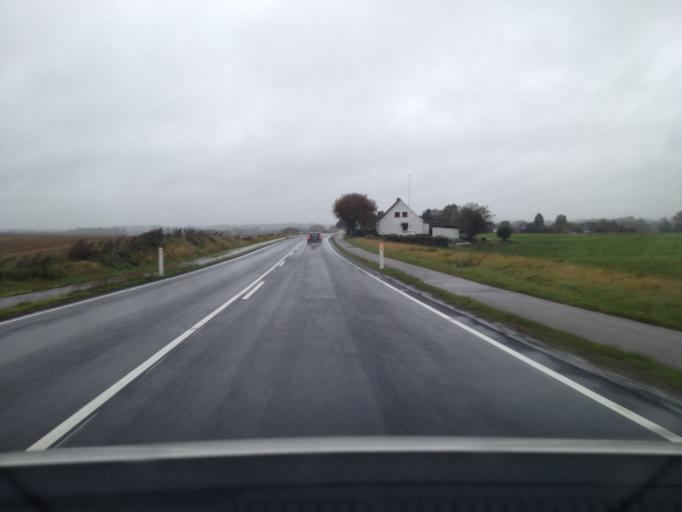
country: DK
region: Zealand
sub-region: Holbaek Kommune
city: Tollose
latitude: 55.5377
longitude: 11.7127
